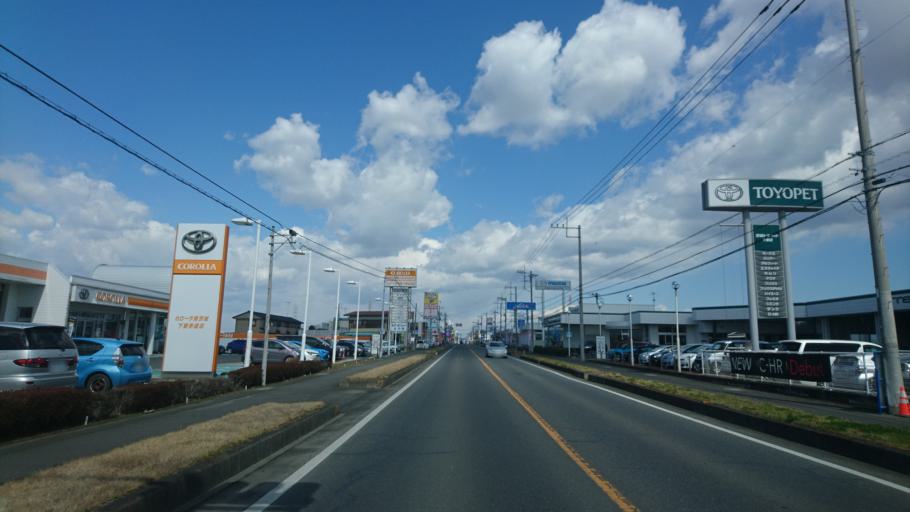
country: JP
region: Ibaraki
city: Ishige
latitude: 36.1644
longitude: 139.9677
